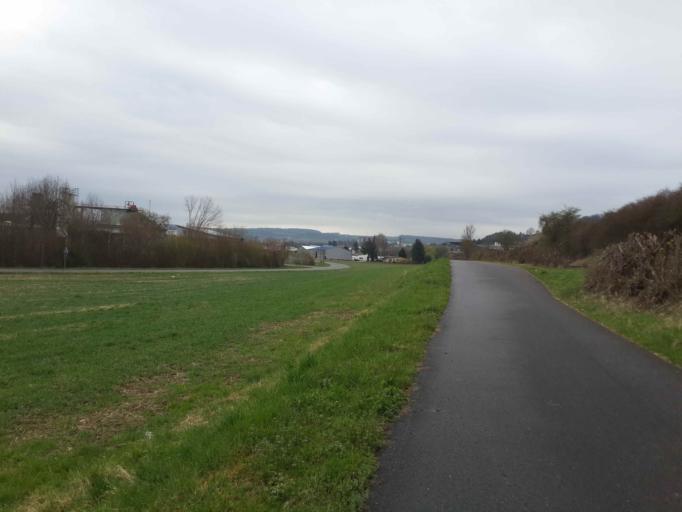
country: DE
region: Baden-Wuerttemberg
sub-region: Regierungsbezirk Stuttgart
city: Bad Mergentheim
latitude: 49.5008
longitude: 9.7473
